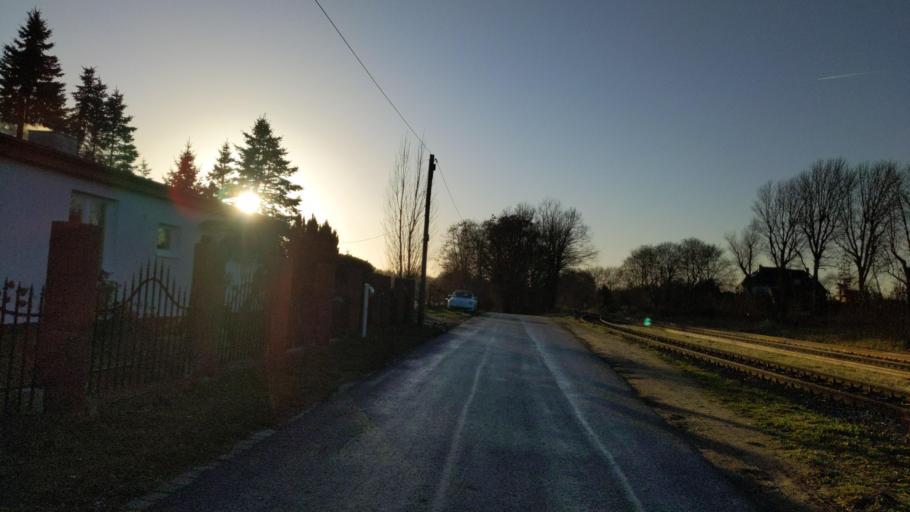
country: DE
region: Mecklenburg-Vorpommern
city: Selmsdorf
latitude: 53.8841
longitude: 10.7918
